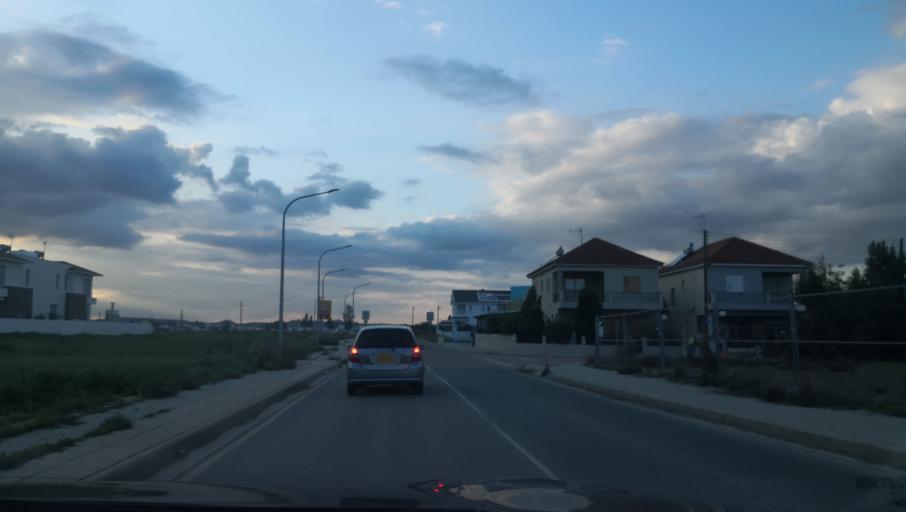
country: CY
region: Lefkosia
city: Tseri
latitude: 35.0987
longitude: 33.3203
